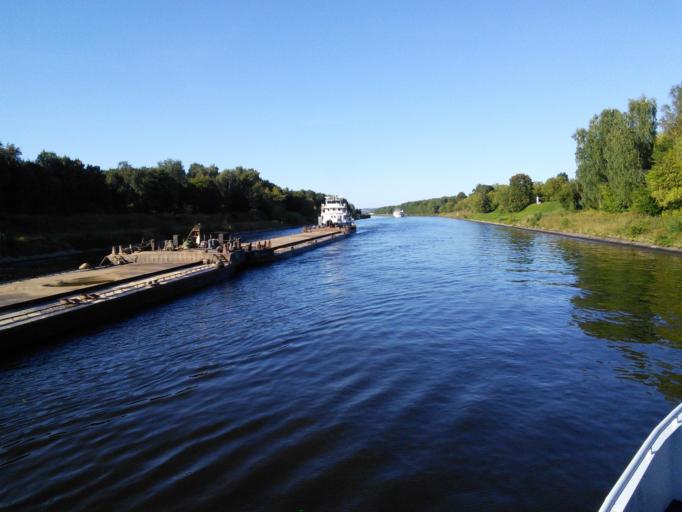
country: RU
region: Moskovskaya
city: Yakhroma
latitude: 56.3231
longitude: 37.4945
